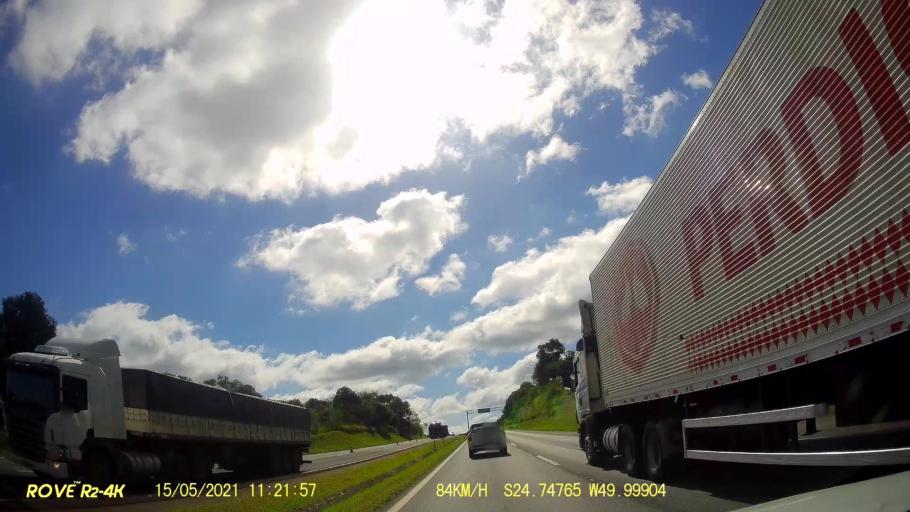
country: BR
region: Parana
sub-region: Castro
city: Castro
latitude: -24.7478
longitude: -49.9990
